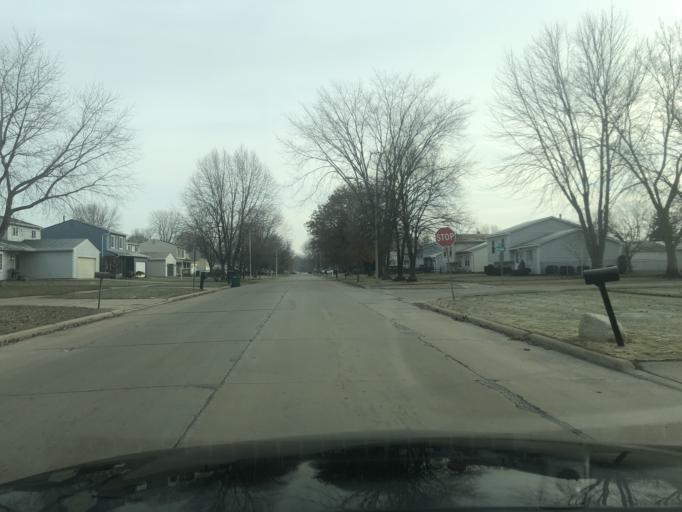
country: US
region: Michigan
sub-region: Wayne County
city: Taylor
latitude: 42.1879
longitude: -83.3205
